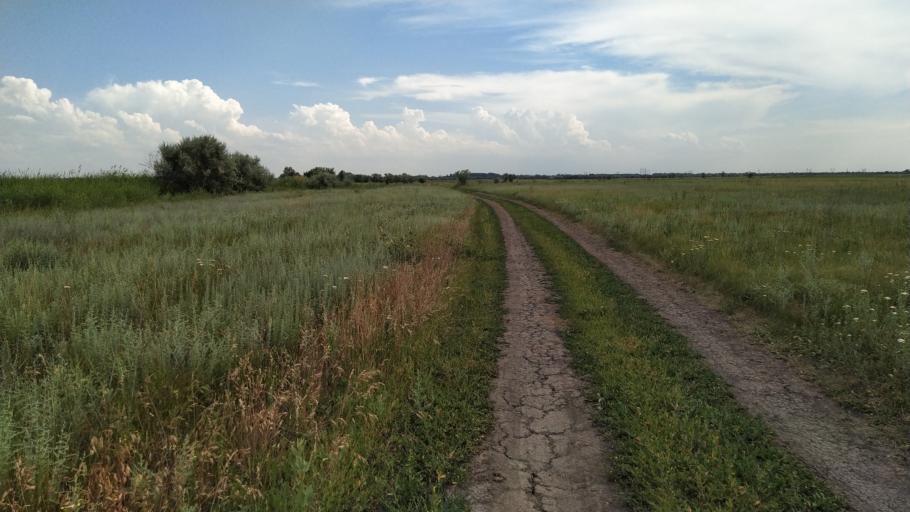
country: RU
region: Rostov
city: Kuleshovka
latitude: 47.1340
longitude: 39.6306
